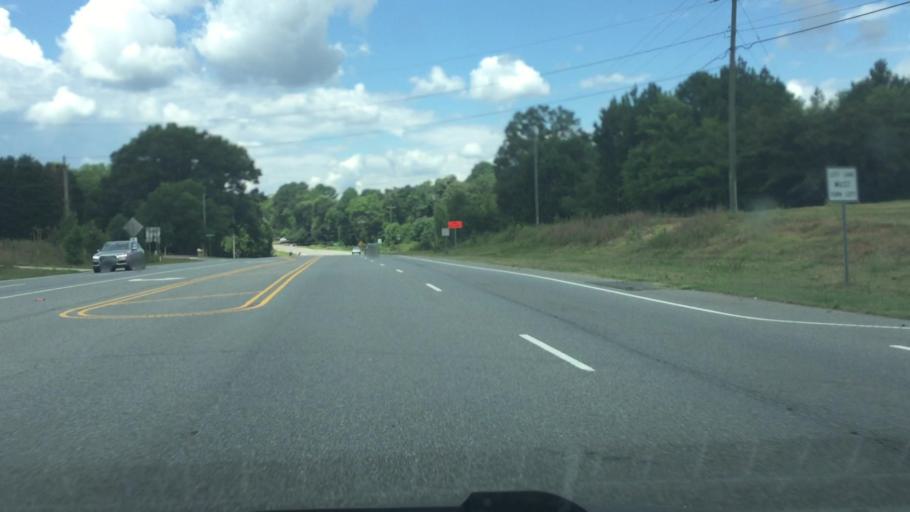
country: US
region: North Carolina
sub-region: Rowan County
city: Enochville
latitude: 35.4904
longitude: -80.6728
